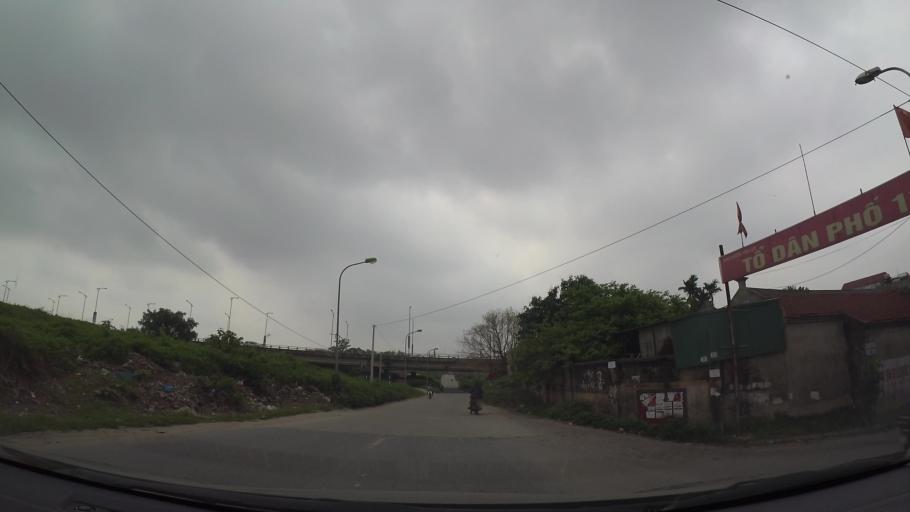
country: VN
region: Ha Noi
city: Trau Quy
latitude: 21.0390
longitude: 105.9360
